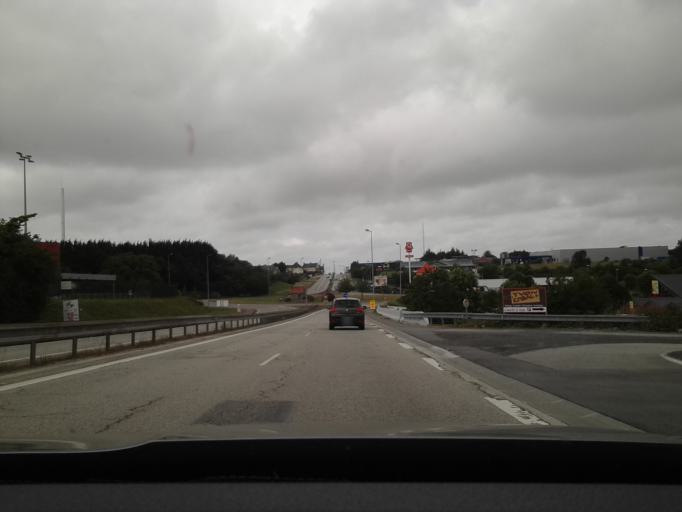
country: FR
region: Lower Normandy
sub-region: Departement de la Manche
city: La Glacerie
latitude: 49.6036
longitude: -1.5984
